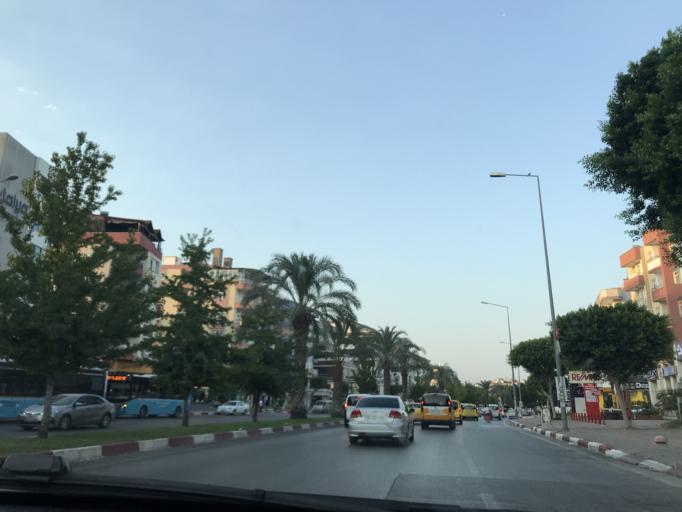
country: TR
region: Antalya
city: Antalya
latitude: 36.8752
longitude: 30.6434
